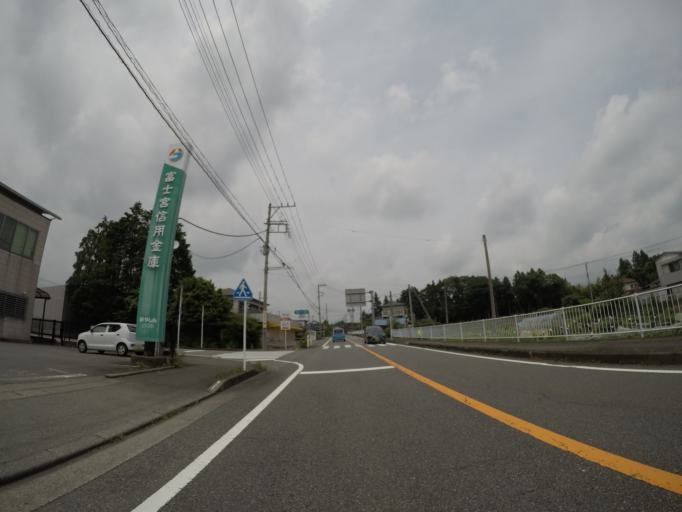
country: JP
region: Shizuoka
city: Fujinomiya
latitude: 35.3019
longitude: 138.5939
